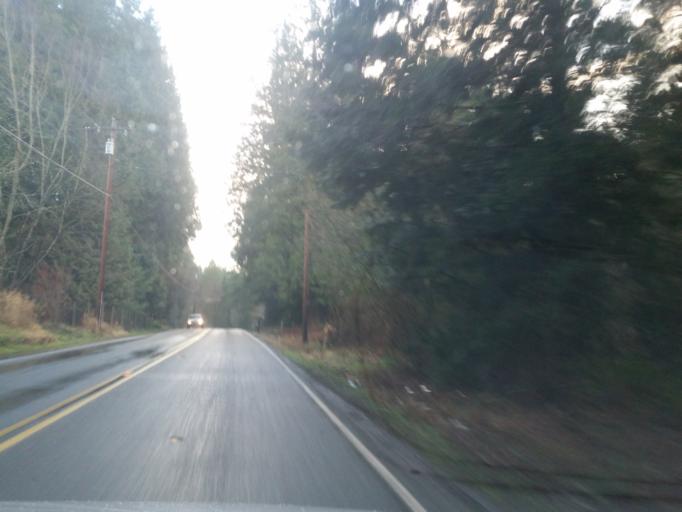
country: US
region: Washington
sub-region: Snohomish County
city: Maltby
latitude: 47.8182
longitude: -122.0929
